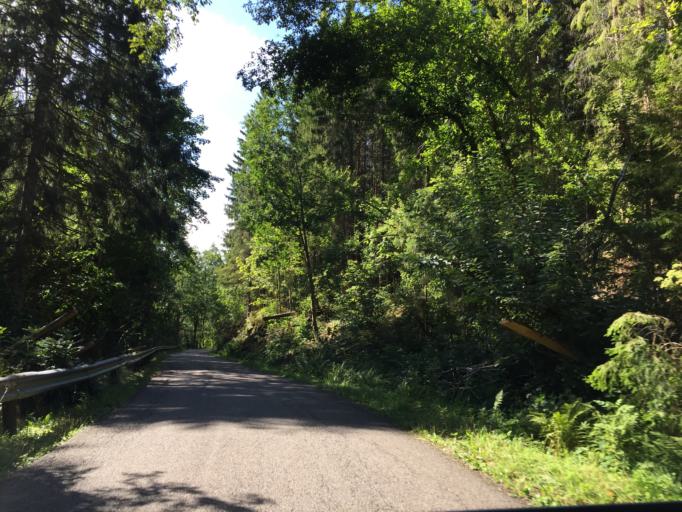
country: NO
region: Vestfold
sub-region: Hof
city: Hof
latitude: 59.4804
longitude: 10.1495
